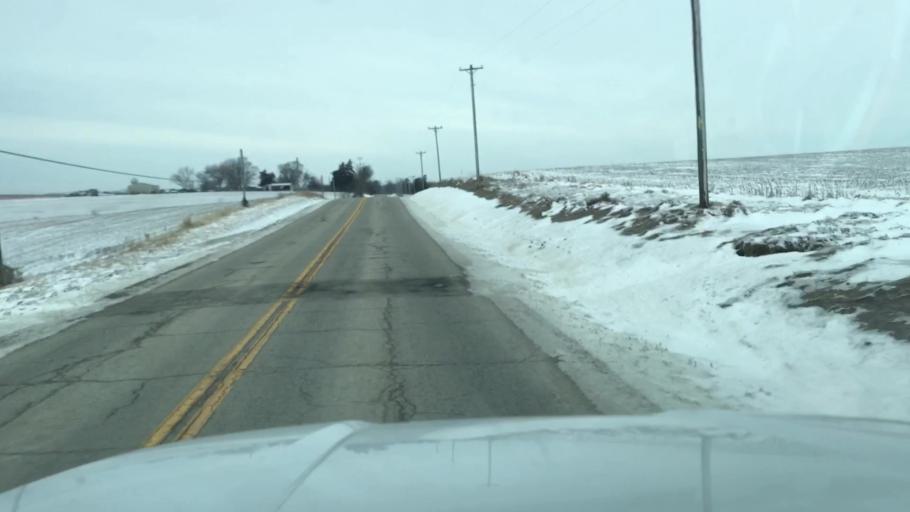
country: US
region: Missouri
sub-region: Andrew County
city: Savannah
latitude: 40.0250
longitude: -94.9575
